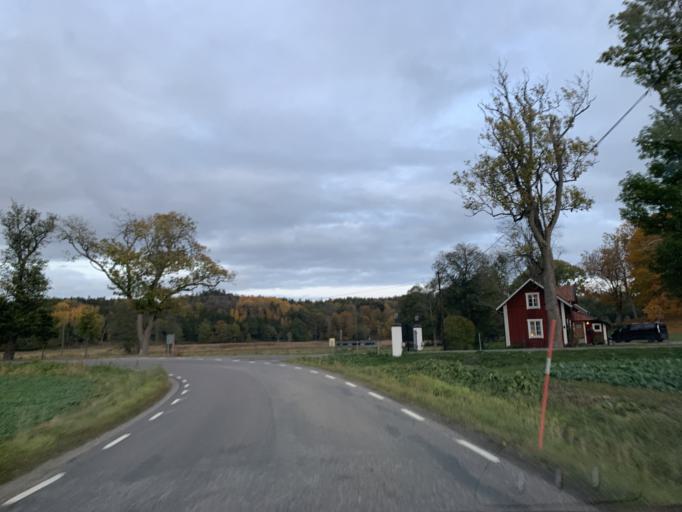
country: SE
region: Stockholm
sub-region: Nynashamns Kommun
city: Osmo
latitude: 58.9592
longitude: 17.7670
